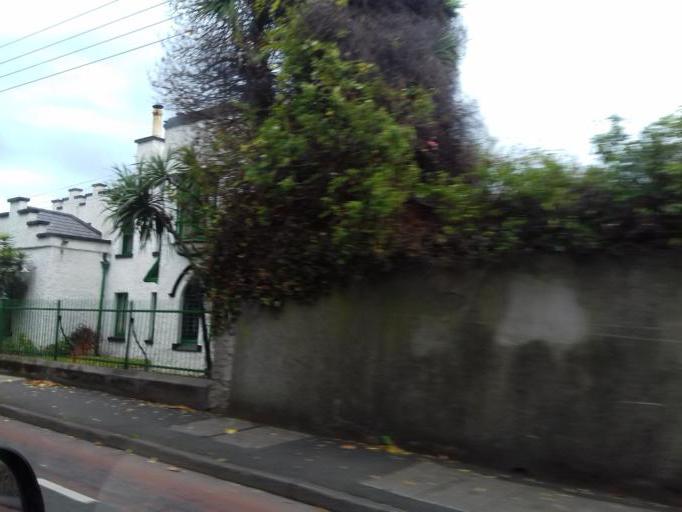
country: IE
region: Leinster
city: Shankill
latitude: 53.2254
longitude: -6.1252
